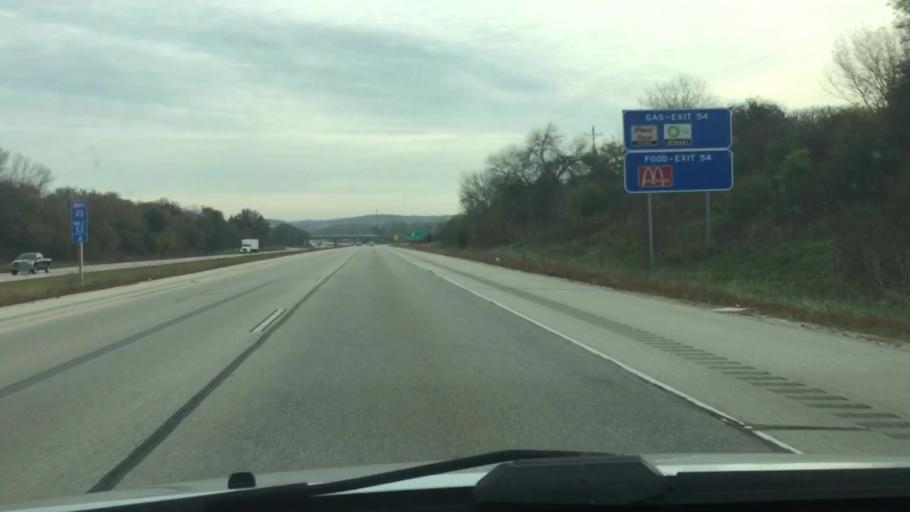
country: US
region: Wisconsin
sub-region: Waukesha County
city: Muskego
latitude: 42.9314
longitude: -88.1685
